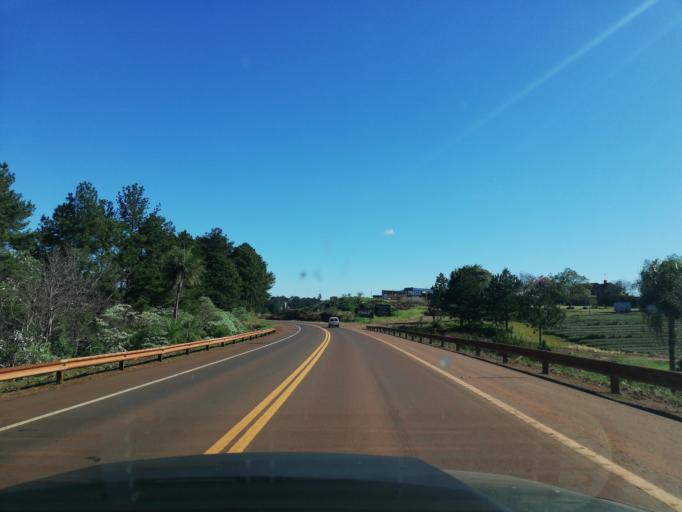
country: AR
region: Misiones
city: Aristobulo del Valle
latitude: -27.0891
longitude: -54.8604
